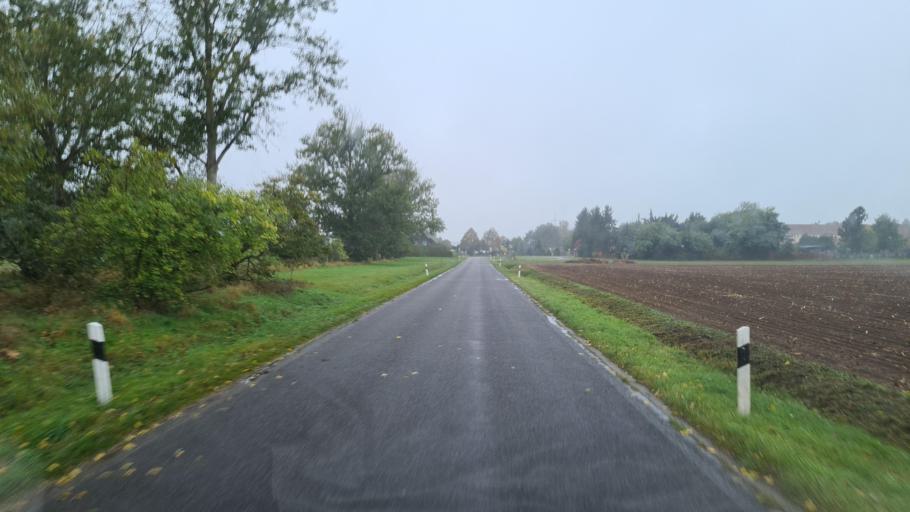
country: DE
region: Brandenburg
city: Furstenwalde
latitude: 52.4316
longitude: 14.0213
